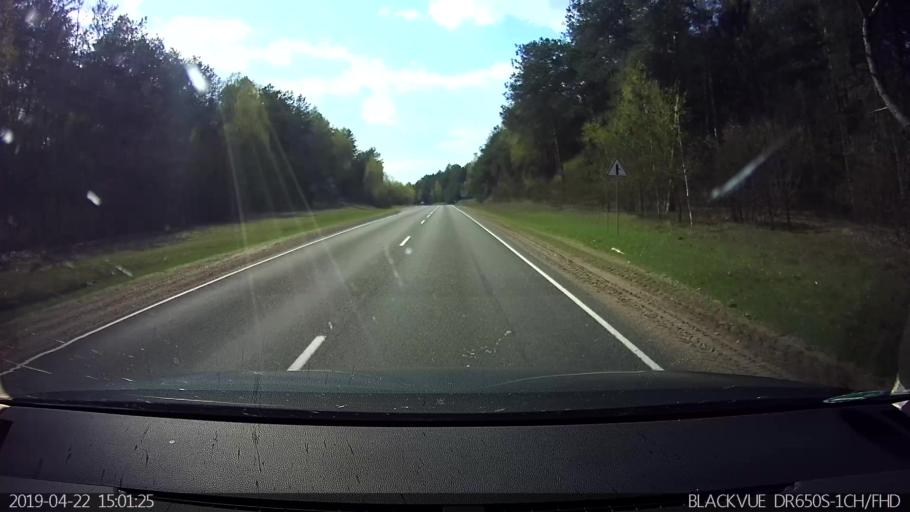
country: BY
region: Brest
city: Zhabinka
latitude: 52.3527
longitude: 23.9660
